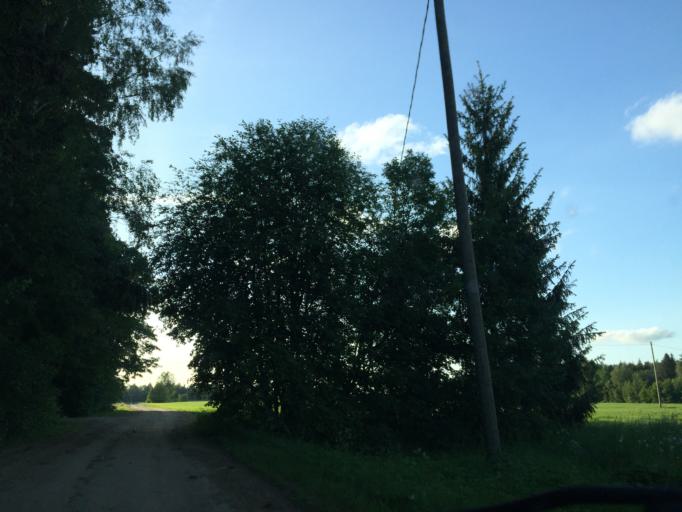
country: LV
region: Koceni
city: Koceni
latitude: 57.4730
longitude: 25.2625
